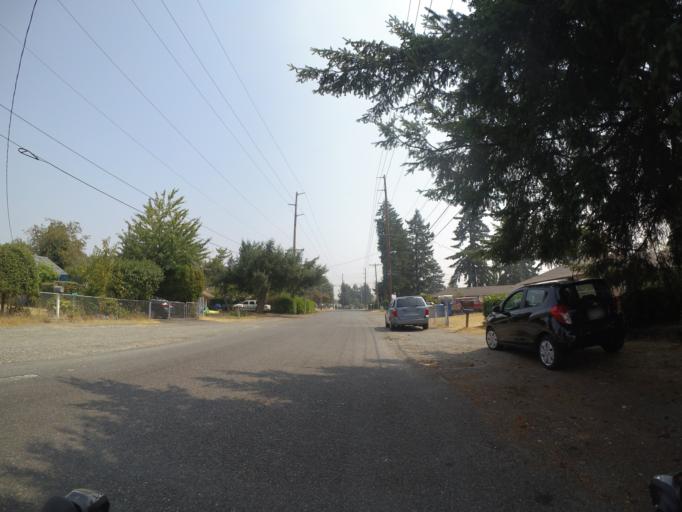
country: US
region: Washington
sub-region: Pierce County
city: Lakewood
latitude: 47.1567
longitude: -122.5115
